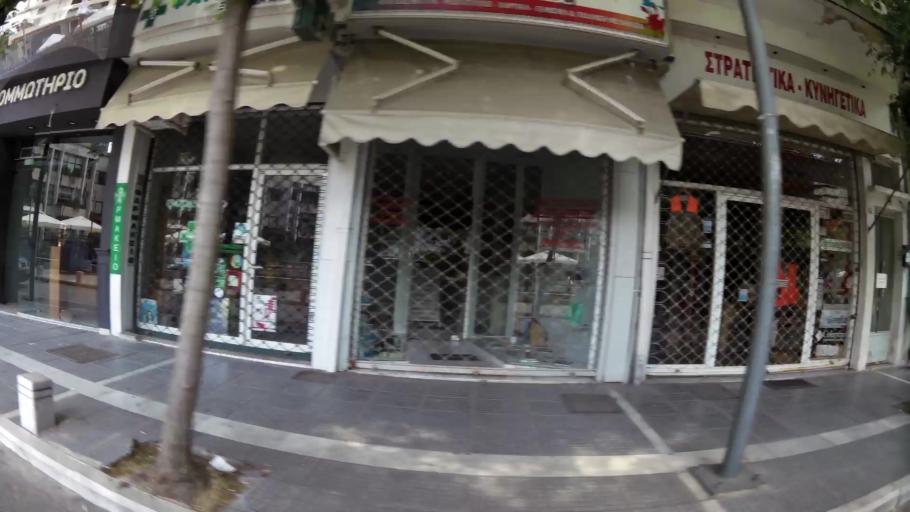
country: GR
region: Central Macedonia
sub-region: Nomos Pierias
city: Katerini
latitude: 40.2731
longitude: 22.5073
